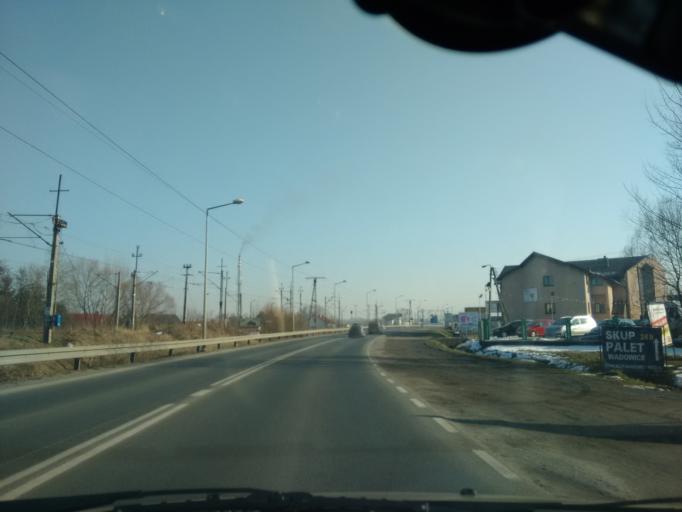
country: PL
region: Lesser Poland Voivodeship
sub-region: Powiat wadowicki
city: Wadowice
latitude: 49.8896
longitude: 19.4964
